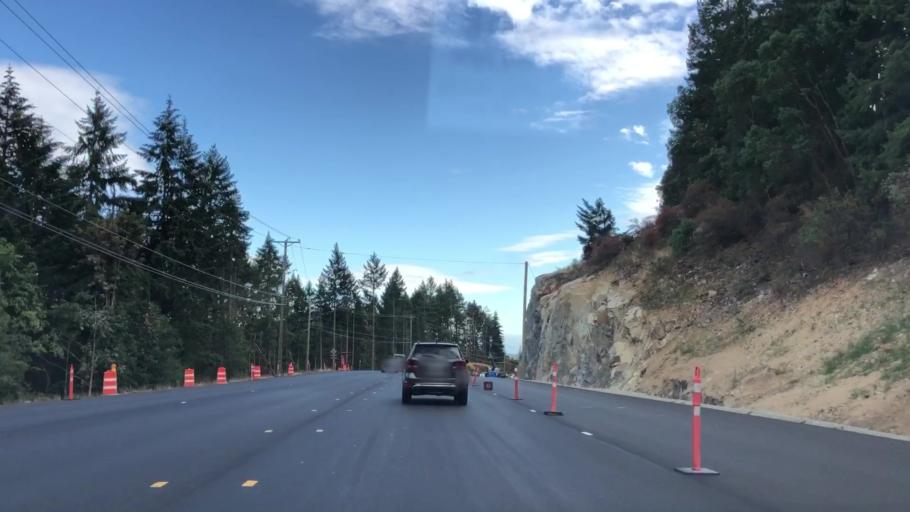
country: CA
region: British Columbia
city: Langford
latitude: 48.5233
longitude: -123.5553
